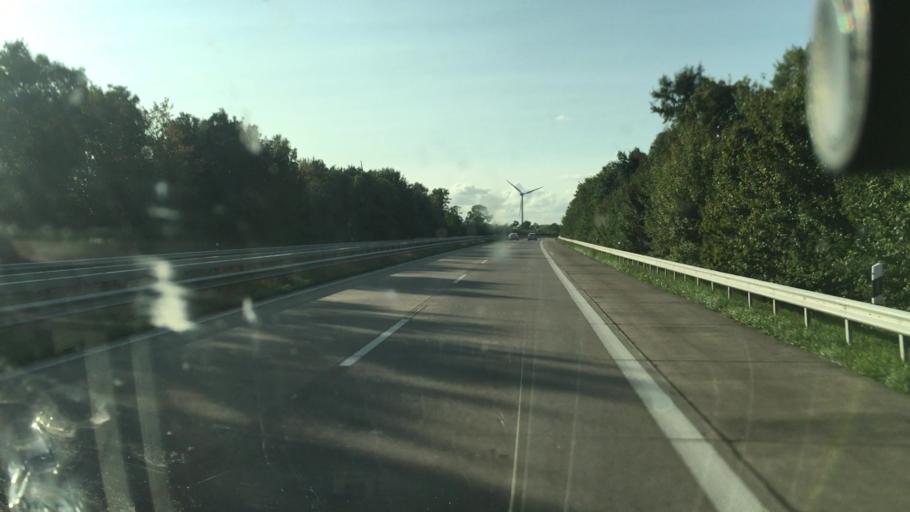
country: DE
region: Lower Saxony
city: Bockhorn
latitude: 53.4330
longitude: 8.0473
